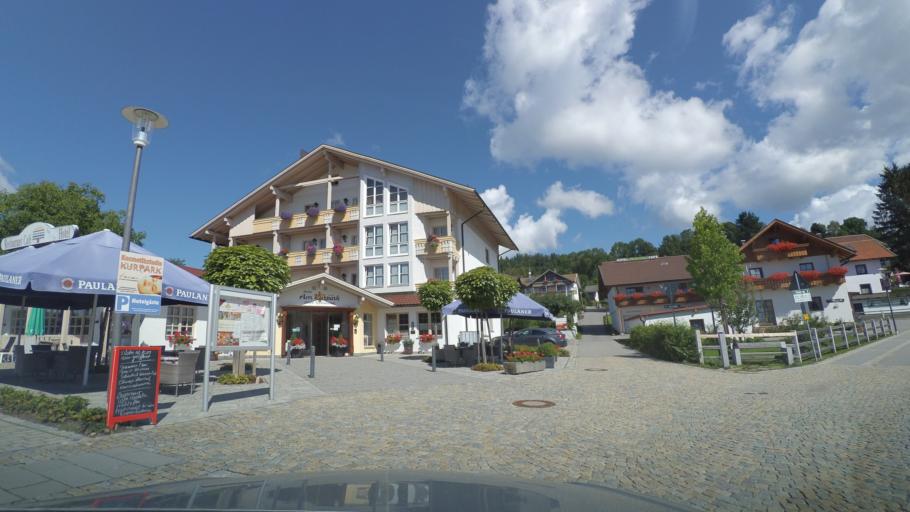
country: DE
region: Bavaria
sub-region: Lower Bavaria
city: Bodenmais
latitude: 49.0701
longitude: 13.0964
